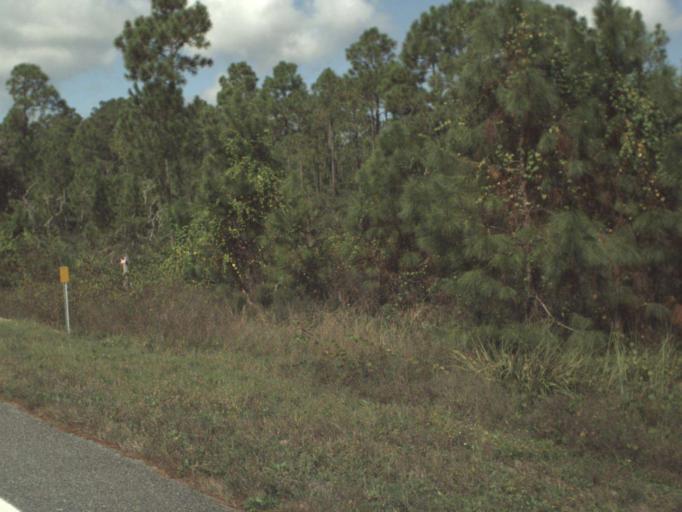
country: US
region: Florida
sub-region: Wakulla County
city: Crawfordville
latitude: 29.9232
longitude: -84.4126
